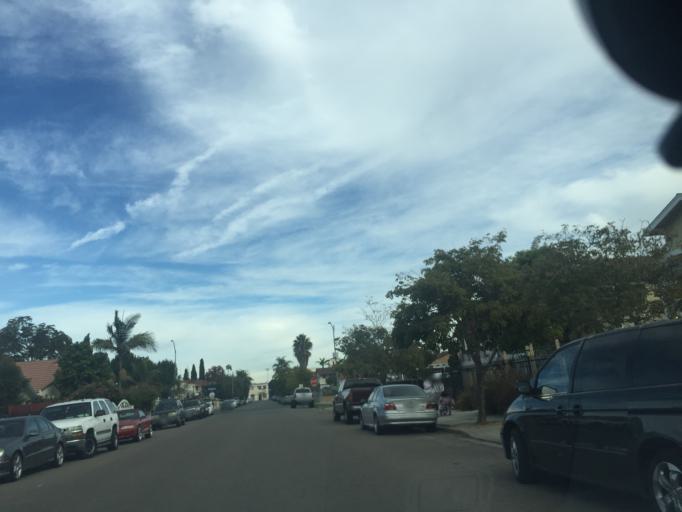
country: US
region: California
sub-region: San Diego County
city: Lemon Grove
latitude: 32.7524
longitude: -117.0987
